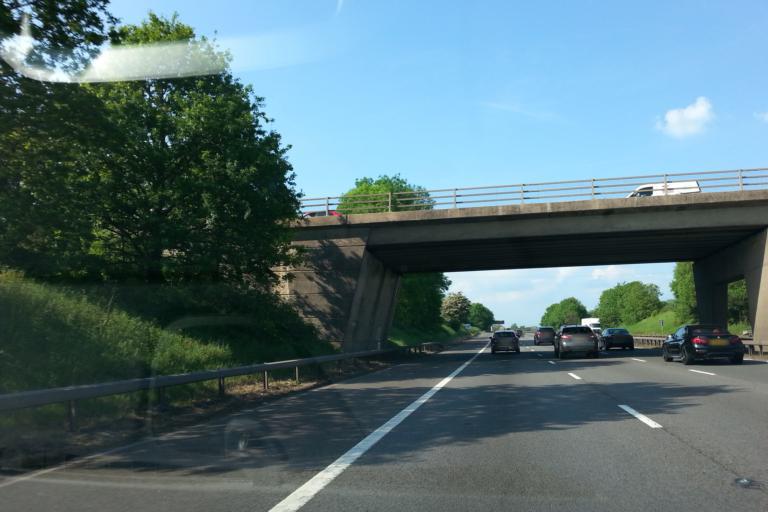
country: GB
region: England
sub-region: Leicestershire
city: Hinckley
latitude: 52.4953
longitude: -1.3850
